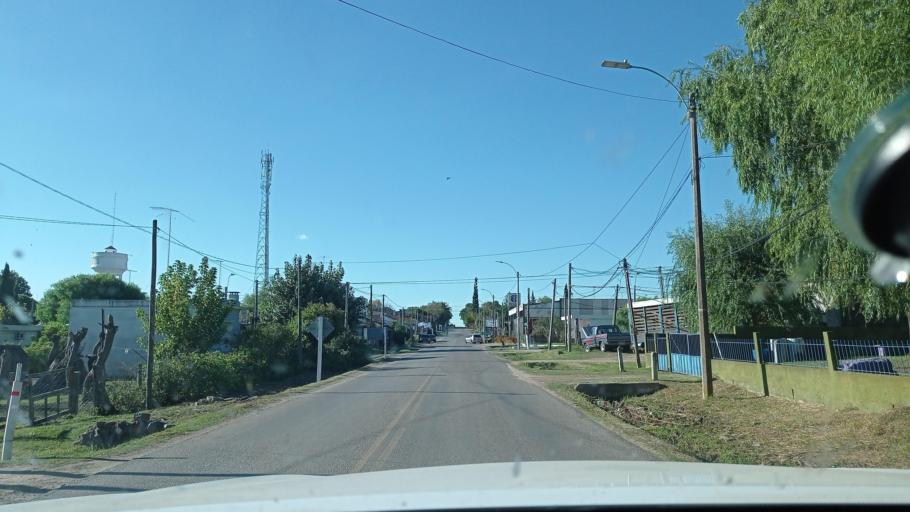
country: UY
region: Canelones
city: Tala
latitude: -34.3478
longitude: -55.7601
